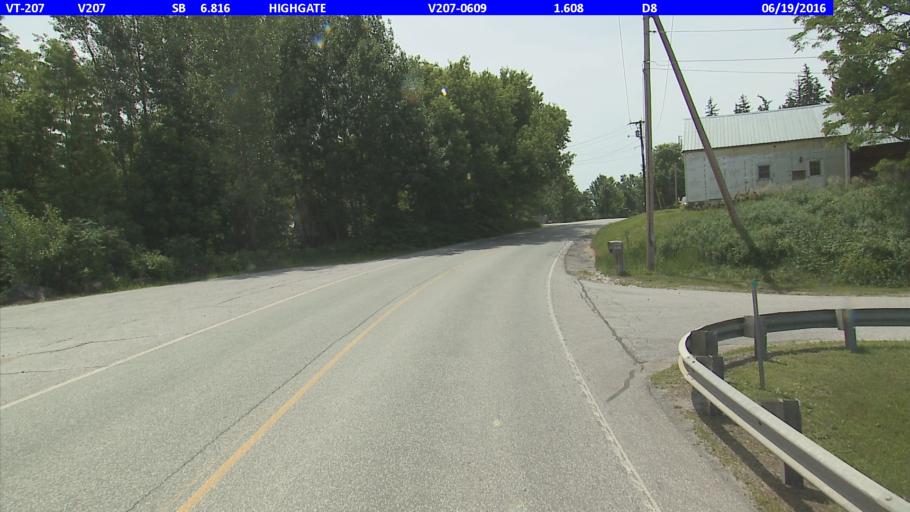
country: US
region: Vermont
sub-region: Franklin County
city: Swanton
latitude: 44.9336
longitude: -73.0486
